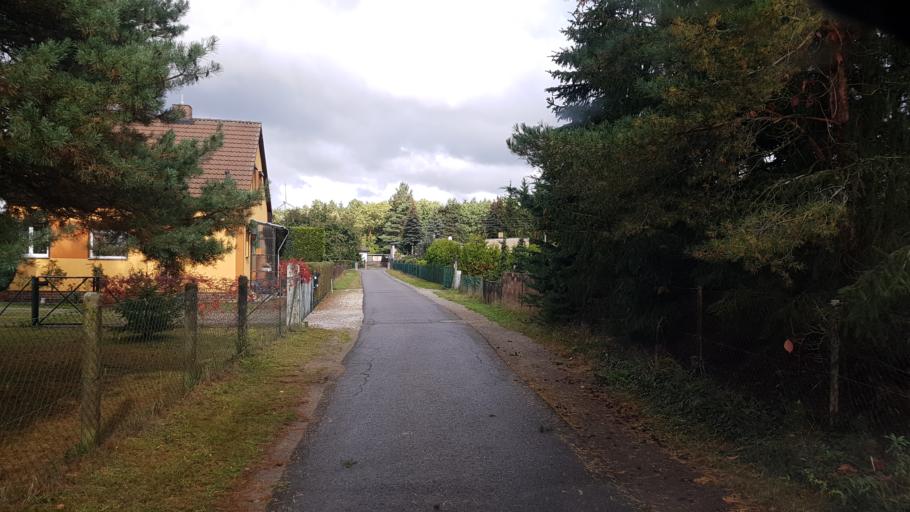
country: DE
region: Brandenburg
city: Grossraschen
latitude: 51.6033
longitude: 14.0023
